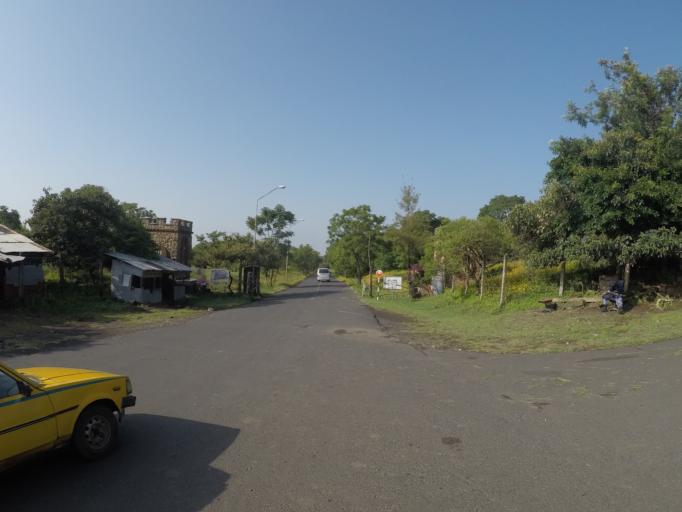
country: ET
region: Amhara
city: Gondar
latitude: 12.5198
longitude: 37.4298
